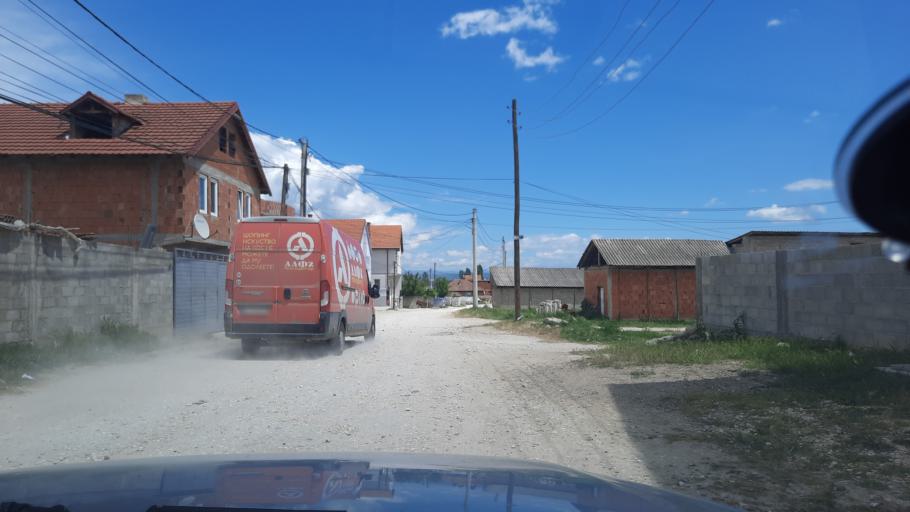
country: MK
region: Studenicani
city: Studenichani
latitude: 41.9237
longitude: 21.5371
